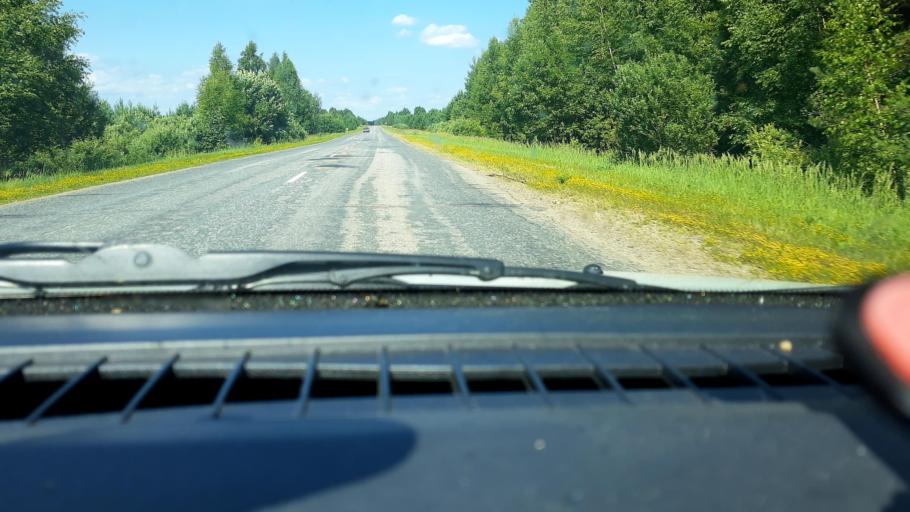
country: RU
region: Nizjnij Novgorod
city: Tonkino
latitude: 57.3104
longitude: 46.4667
